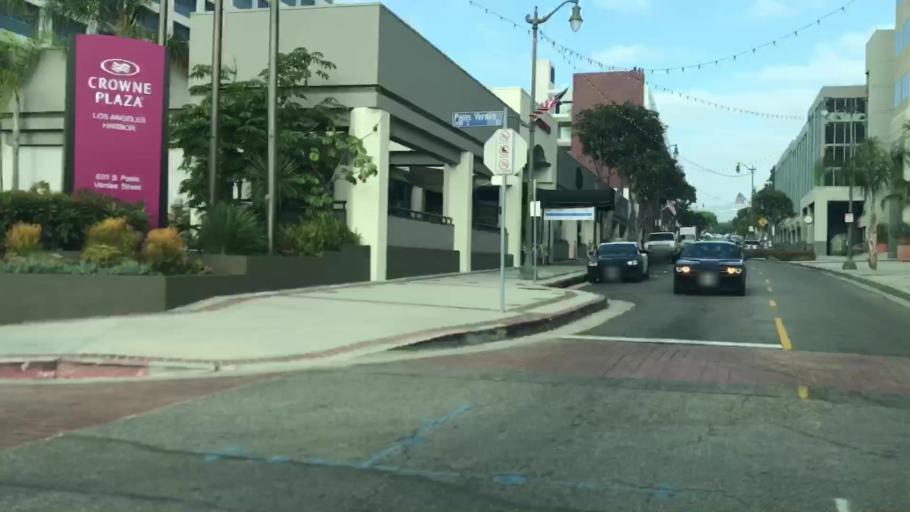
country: US
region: California
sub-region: Los Angeles County
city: San Pedro
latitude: 33.7388
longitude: -118.2810
